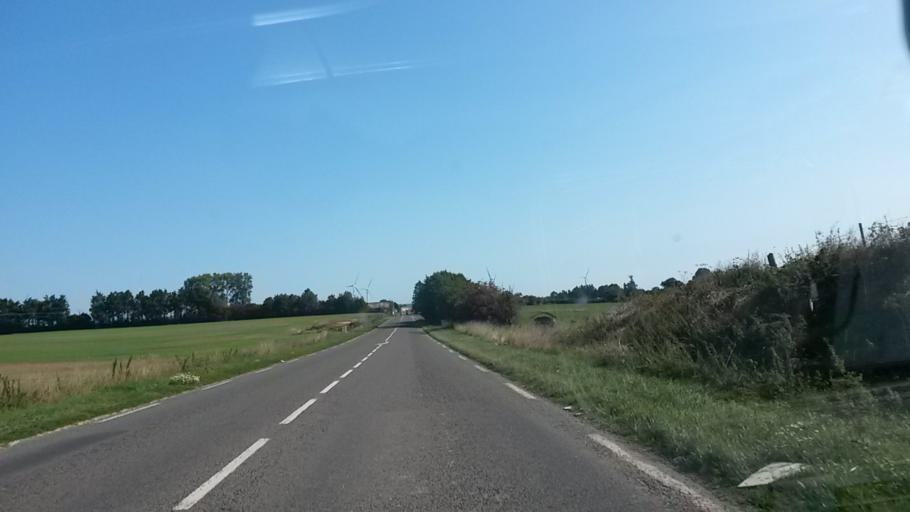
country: FR
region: Picardie
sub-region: Departement de l'Aisne
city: Guise
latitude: 49.9164
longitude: 3.6679
